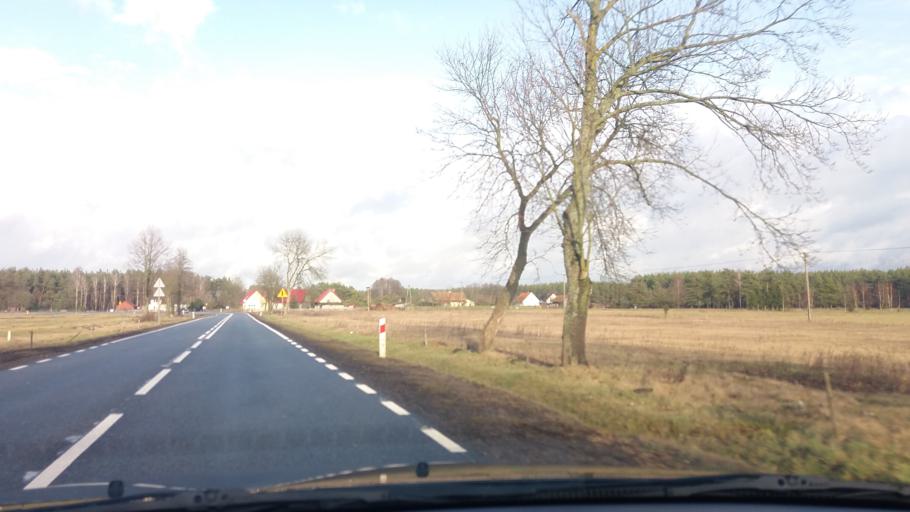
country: PL
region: Masovian Voivodeship
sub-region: Powiat przasnyski
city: Chorzele
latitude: 53.2906
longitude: 20.9141
